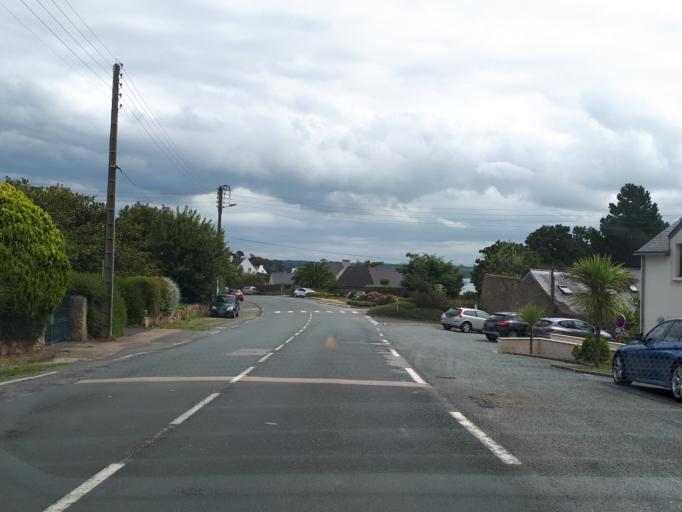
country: FR
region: Brittany
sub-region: Departement du Finistere
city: Carantec
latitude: 48.6656
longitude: -3.9067
